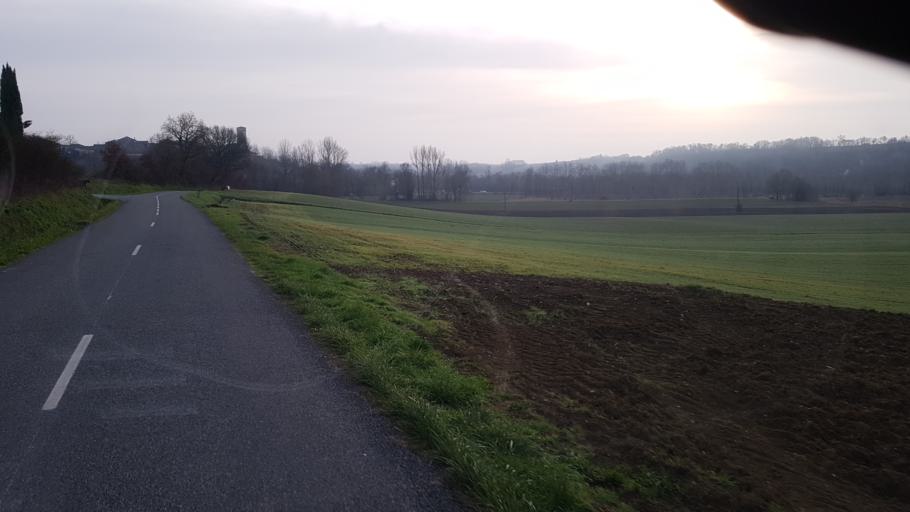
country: FR
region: Midi-Pyrenees
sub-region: Departement du Tarn
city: Cahuzac-sur-Vere
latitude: 43.9885
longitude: 1.8348
